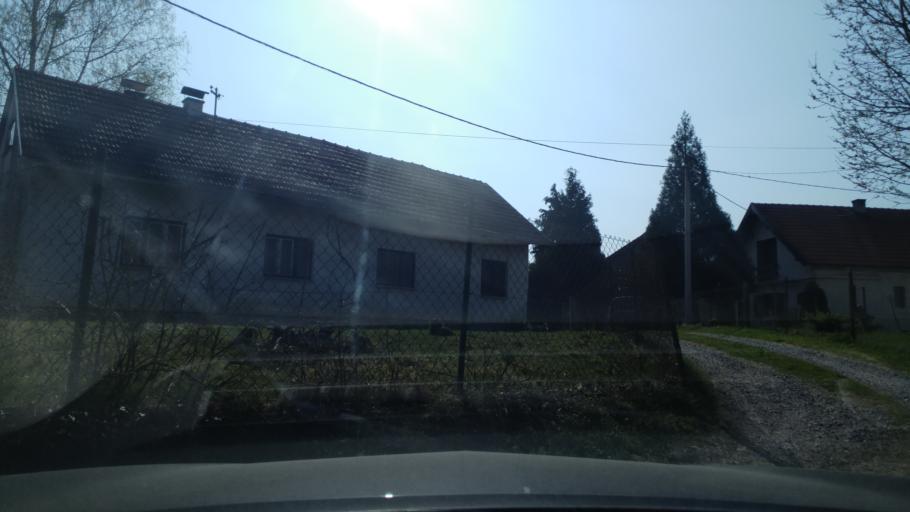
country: SI
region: Bistrica ob Sotli
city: Bistrica ob Sotli
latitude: 46.0031
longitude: 15.7171
